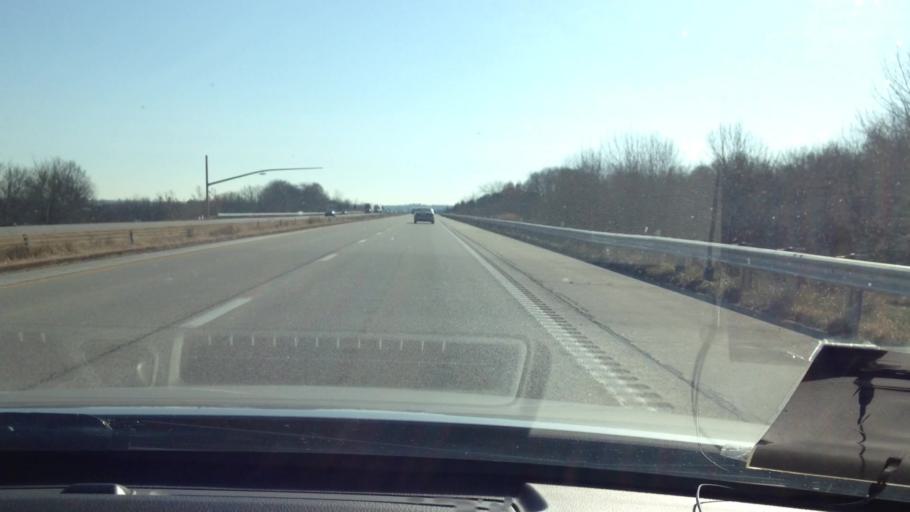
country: US
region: Missouri
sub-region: Platte County
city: Platte City
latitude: 39.4175
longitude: -94.7898
